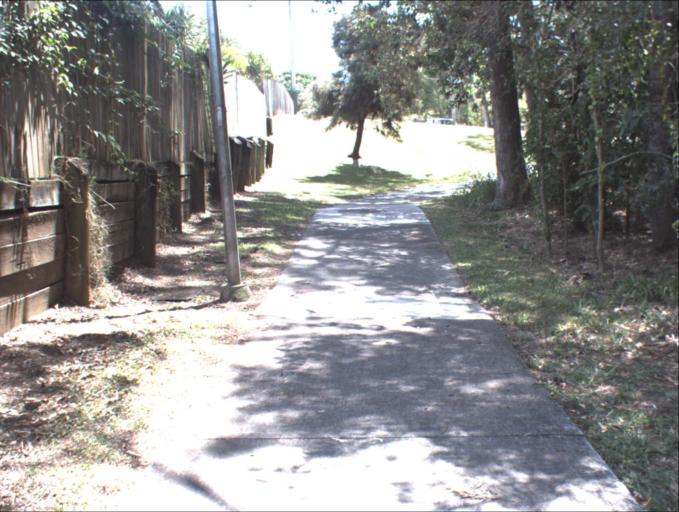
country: AU
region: Queensland
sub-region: Logan
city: Slacks Creek
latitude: -27.6399
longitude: 153.1575
